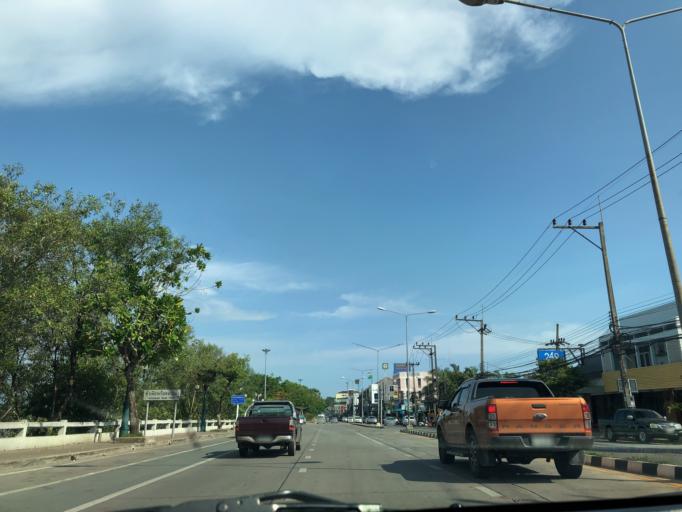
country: TH
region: Krabi
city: Krabi
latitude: 8.0683
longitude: 98.9168
